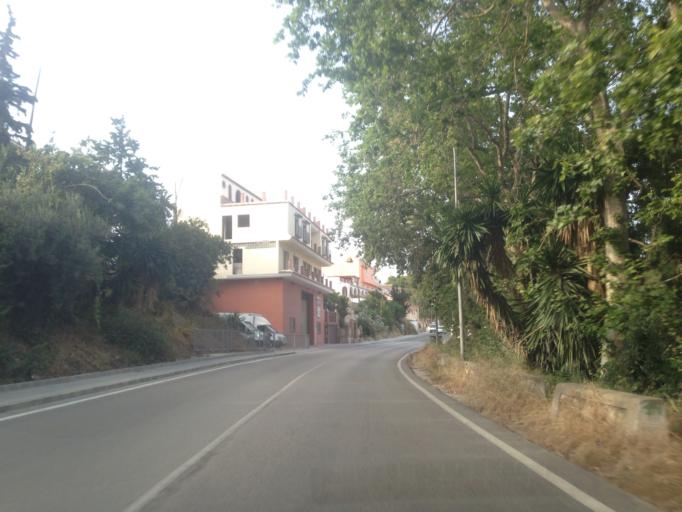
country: ES
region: Andalusia
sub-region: Provincia de Malaga
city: Malaga
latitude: 36.7418
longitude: -4.4120
